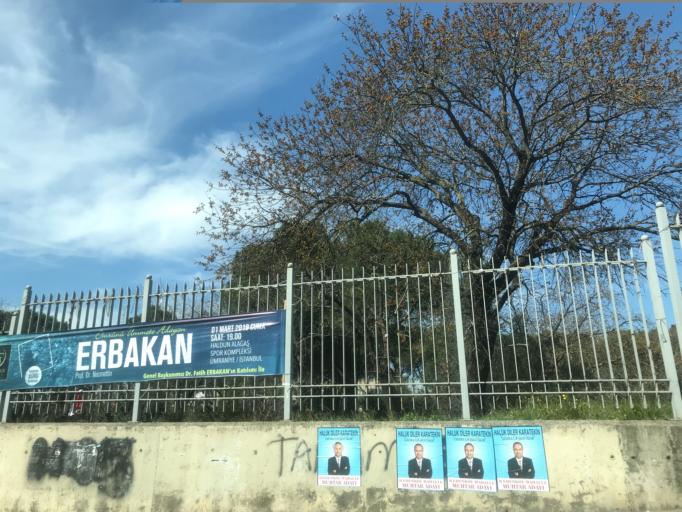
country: TR
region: Istanbul
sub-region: Atasehir
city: Atasehir
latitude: 40.9690
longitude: 29.1063
